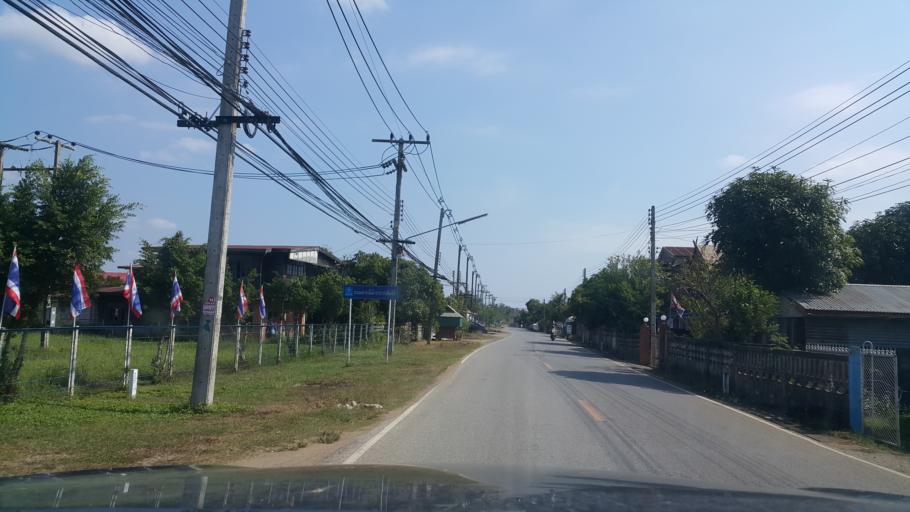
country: TH
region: Sukhothai
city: Thung Saliam
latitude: 17.3224
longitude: 99.5368
